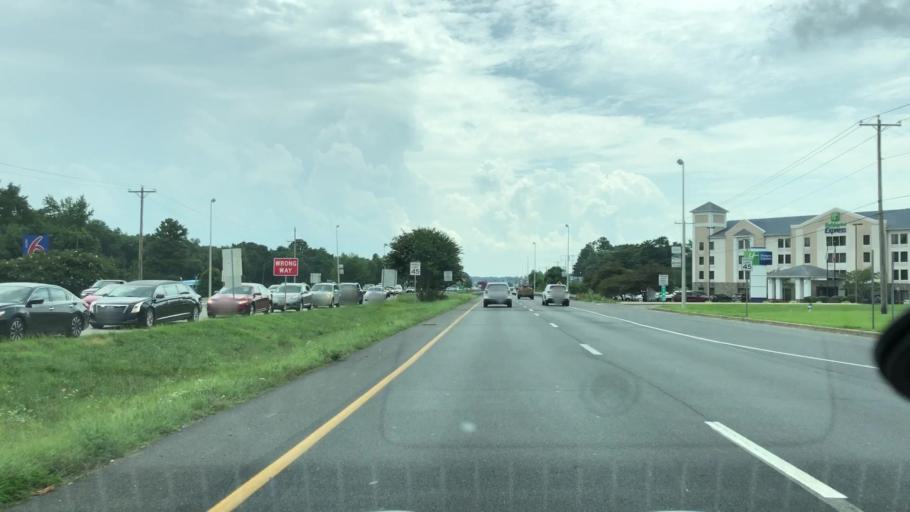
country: US
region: Delaware
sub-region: Sussex County
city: Seaford
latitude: 38.6523
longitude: -75.5945
